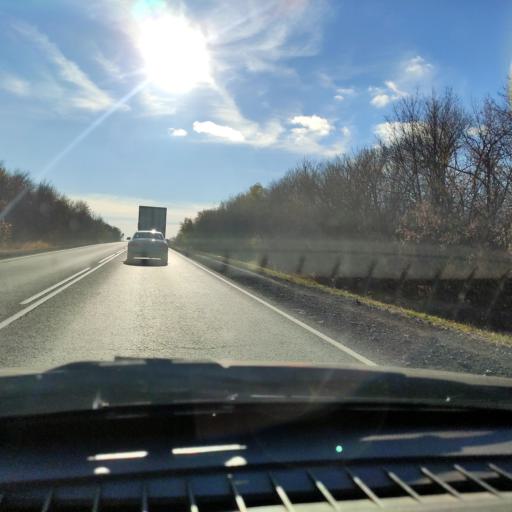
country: RU
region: Samara
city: Zhigulevsk
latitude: 53.3126
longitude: 49.3586
